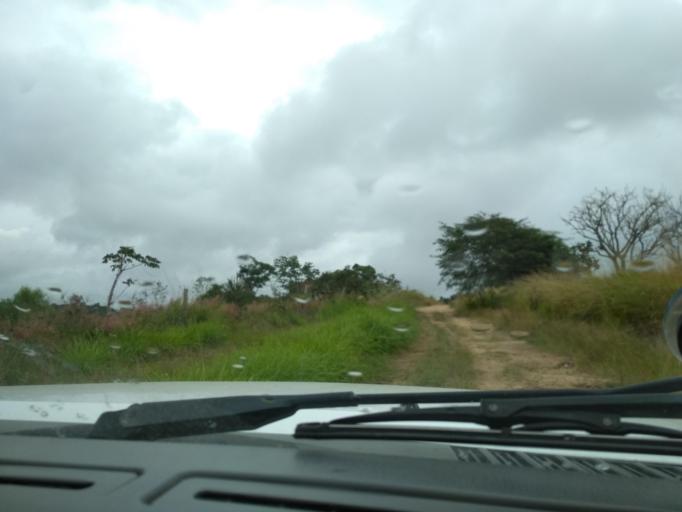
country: MX
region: Veracruz
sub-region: Emiliano Zapata
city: Dos Rios
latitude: 19.5340
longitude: -96.8114
